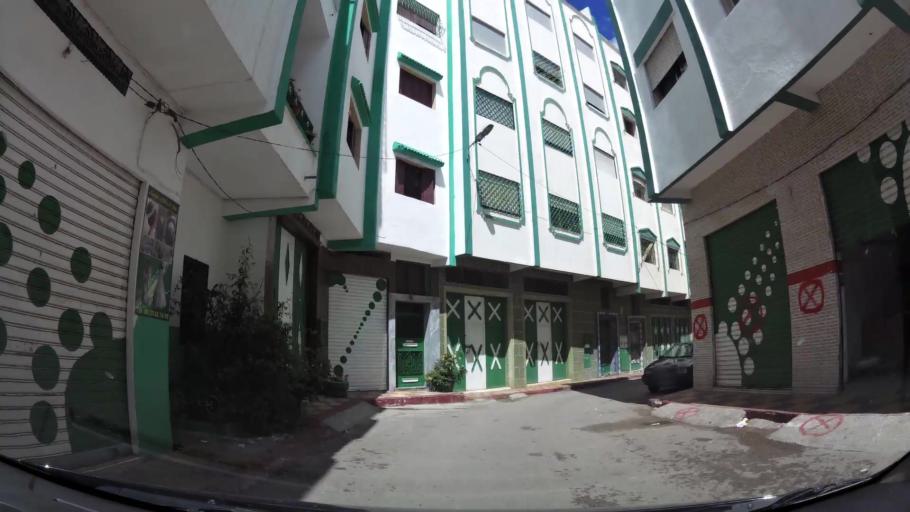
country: MA
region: Tanger-Tetouan
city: Tetouan
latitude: 35.5860
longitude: -5.3467
